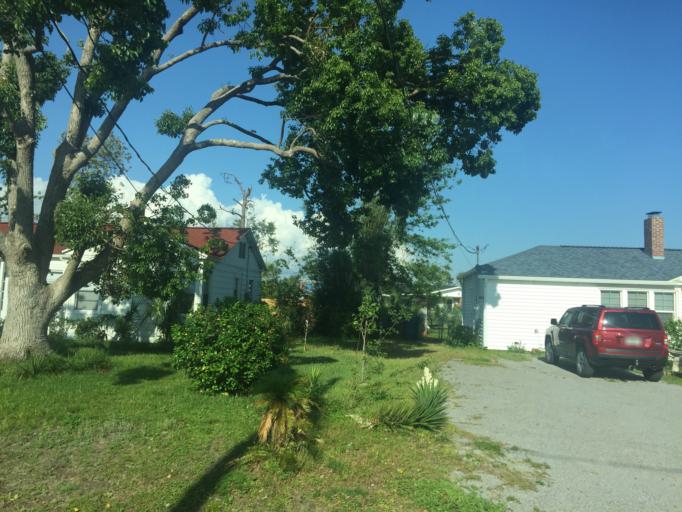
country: US
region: Florida
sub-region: Bay County
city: Panama City
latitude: 30.1538
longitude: -85.6493
